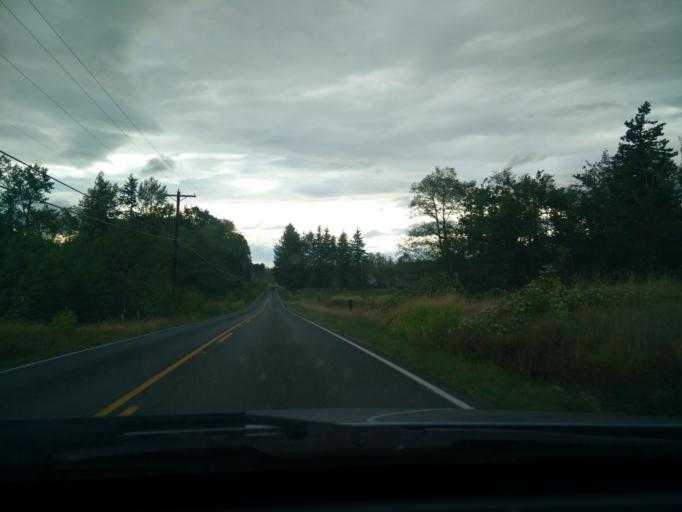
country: US
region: Washington
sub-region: Snohomish County
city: Stanwood
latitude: 48.2685
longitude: -122.3062
